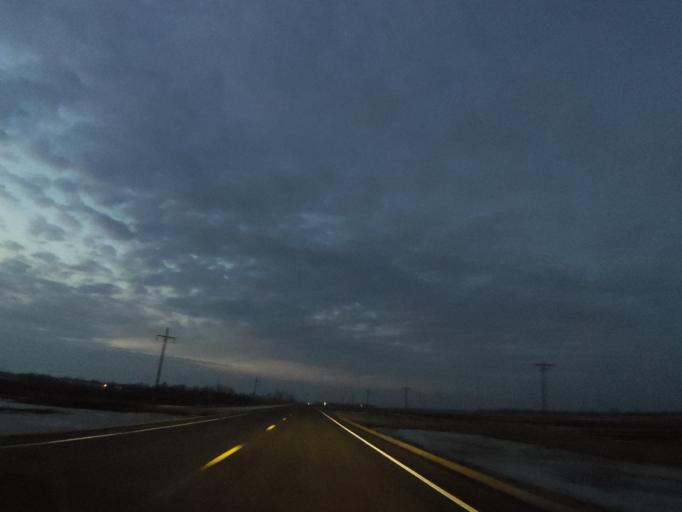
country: US
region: North Dakota
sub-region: Walsh County
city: Park River
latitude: 48.2596
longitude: -97.6225
